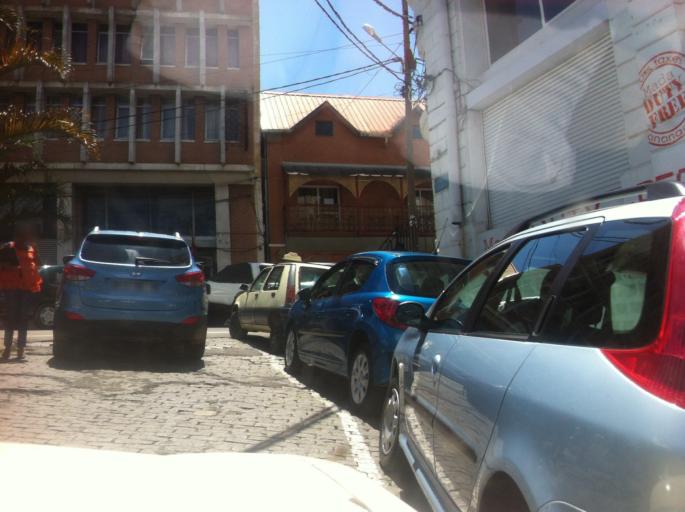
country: MG
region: Analamanga
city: Antananarivo
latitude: -18.9122
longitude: 47.5249
